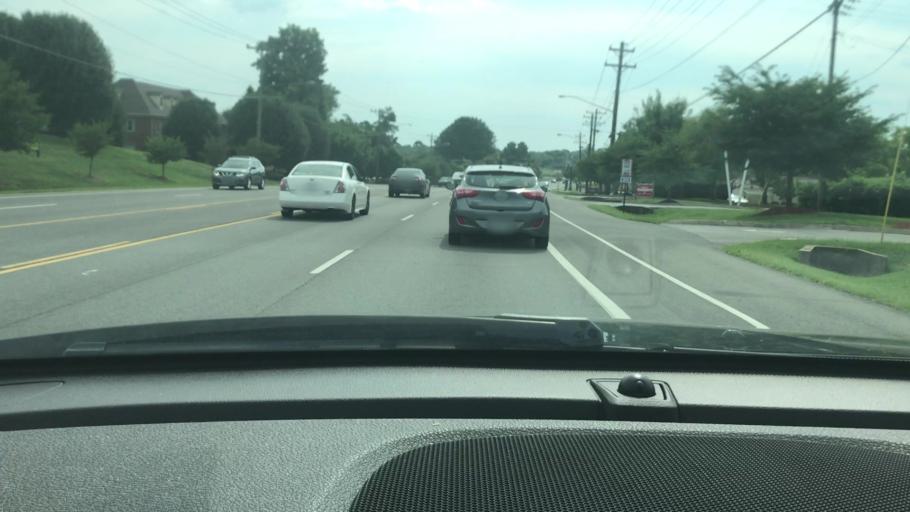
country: US
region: Tennessee
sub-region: Sumner County
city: Hendersonville
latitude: 36.3071
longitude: -86.6074
